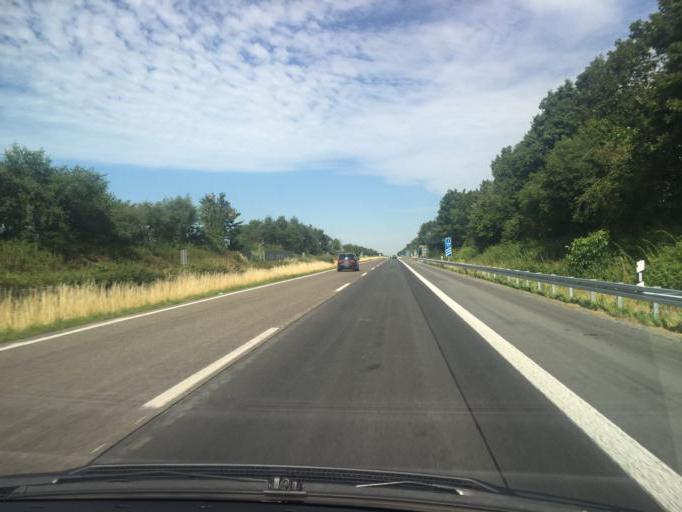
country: DE
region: North Rhine-Westphalia
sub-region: Regierungsbezirk Dusseldorf
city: Weeze
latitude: 51.6538
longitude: 6.1925
